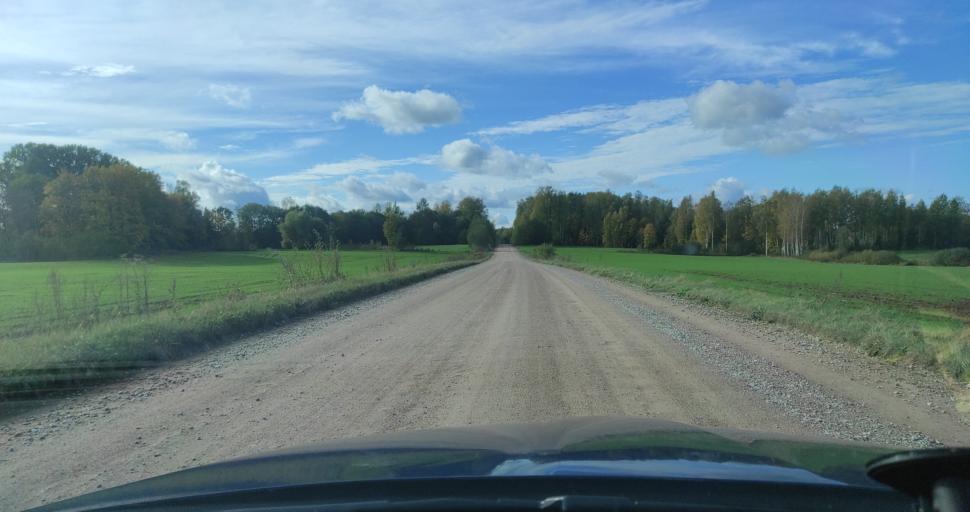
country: LV
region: Jaunpils
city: Jaunpils
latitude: 56.8308
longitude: 22.9827
